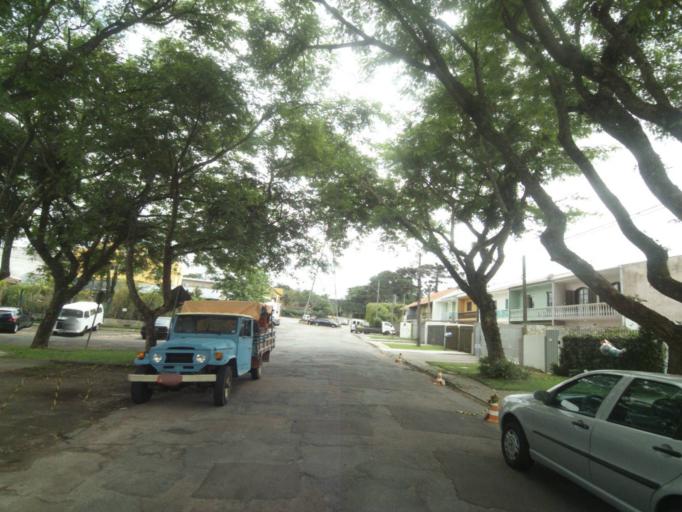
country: BR
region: Parana
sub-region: Curitiba
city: Curitiba
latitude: -25.3863
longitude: -49.2798
